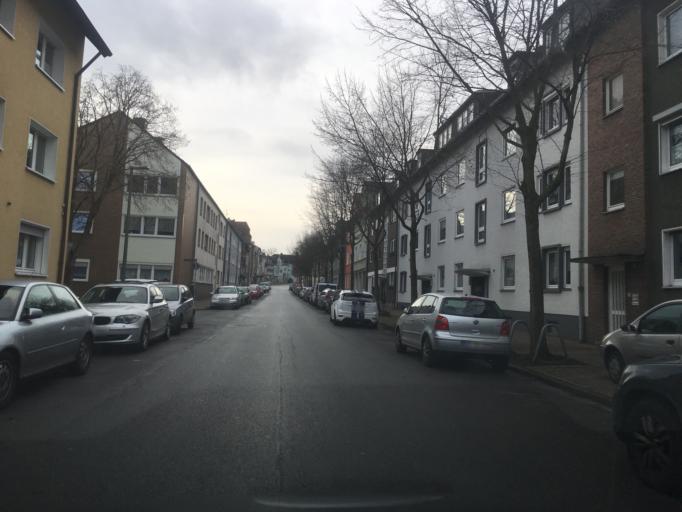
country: DE
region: North Rhine-Westphalia
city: Herten
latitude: 51.5829
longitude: 7.1088
